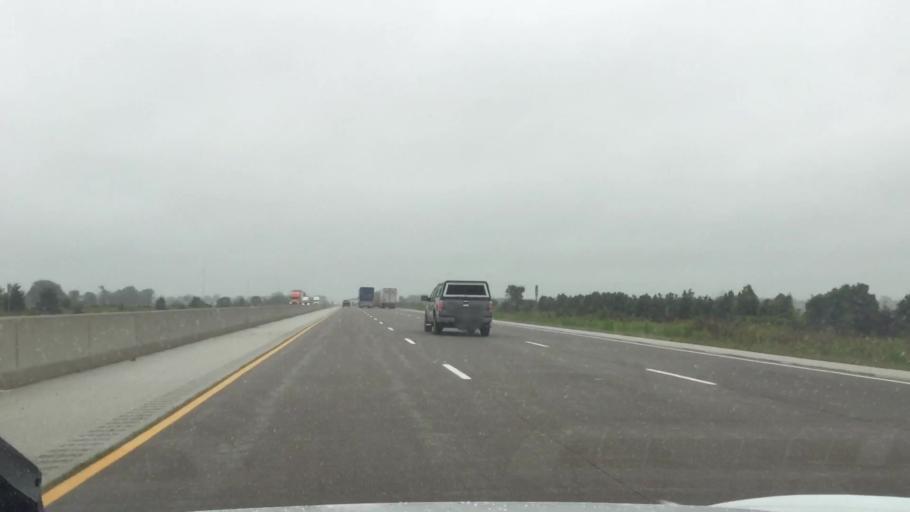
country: US
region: Michigan
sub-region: Wayne County
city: Grosse Pointe
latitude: 42.2373
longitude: -82.7374
